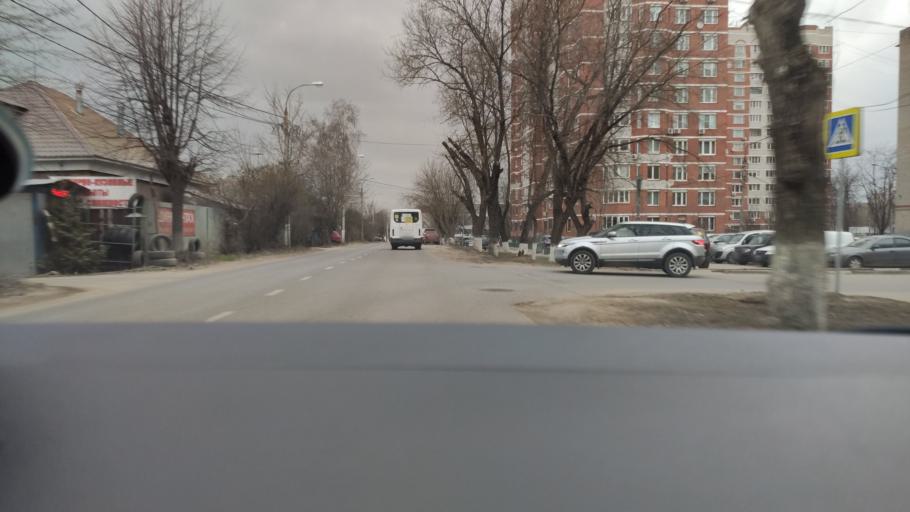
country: RU
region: Moskovskaya
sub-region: Podol'skiy Rayon
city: Podol'sk
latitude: 55.4018
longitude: 37.5551
